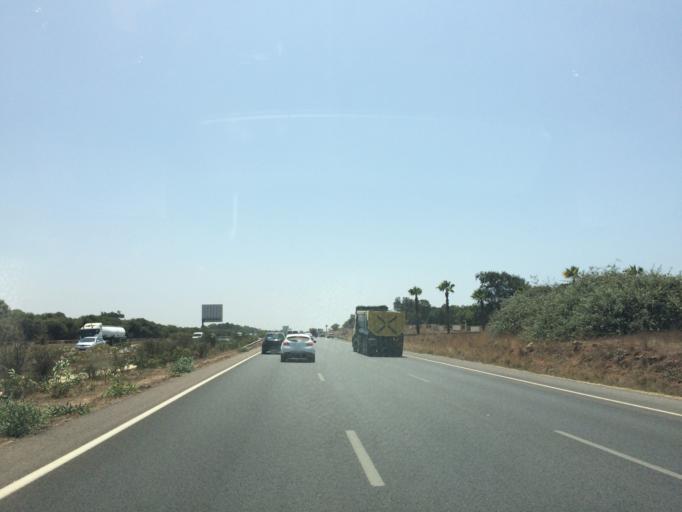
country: MA
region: Rabat-Sale-Zemmour-Zaer
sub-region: Skhirate-Temara
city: Temara
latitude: 33.9482
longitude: -6.9199
